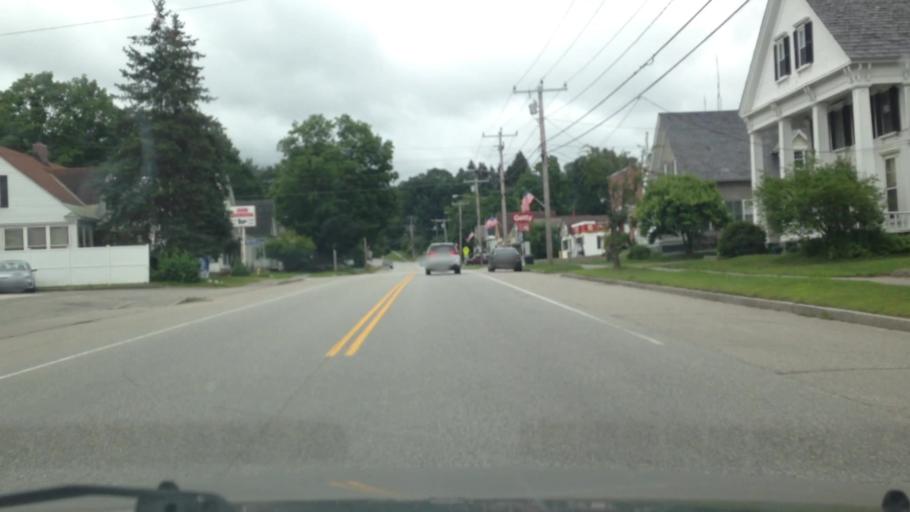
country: US
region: New Hampshire
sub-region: Cheshire County
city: Marlborough
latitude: 42.9061
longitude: -72.2105
